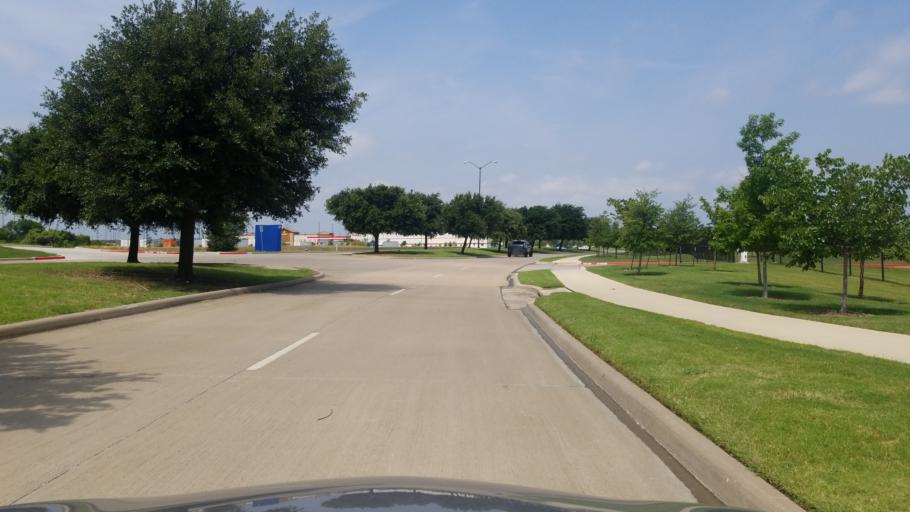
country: US
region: Texas
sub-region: Dallas County
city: Duncanville
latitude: 32.6737
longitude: -96.9649
